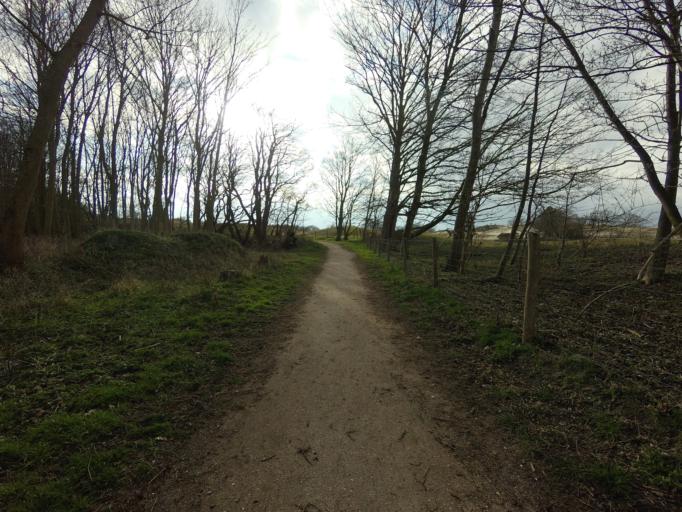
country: NL
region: Zeeland
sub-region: Schouwen-Duiveland
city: Burgh
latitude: 51.6935
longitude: 3.7306
